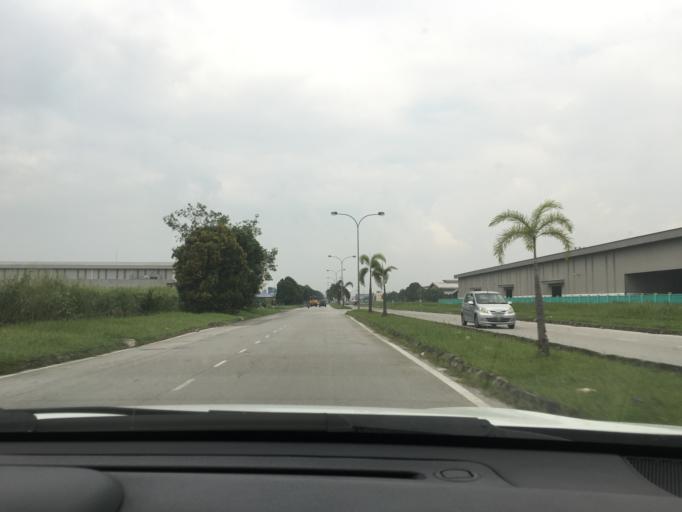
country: MY
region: Selangor
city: Klang
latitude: 3.1374
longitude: 101.4054
